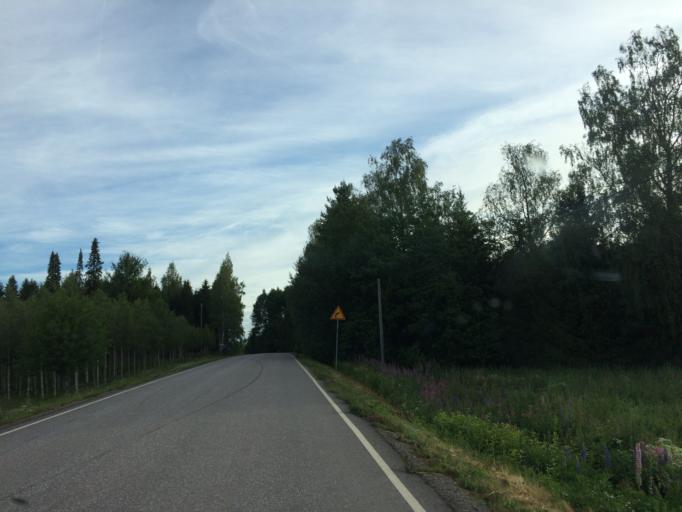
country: FI
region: Haeme
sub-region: Haemeenlinna
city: Janakkala
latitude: 60.8760
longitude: 24.5644
